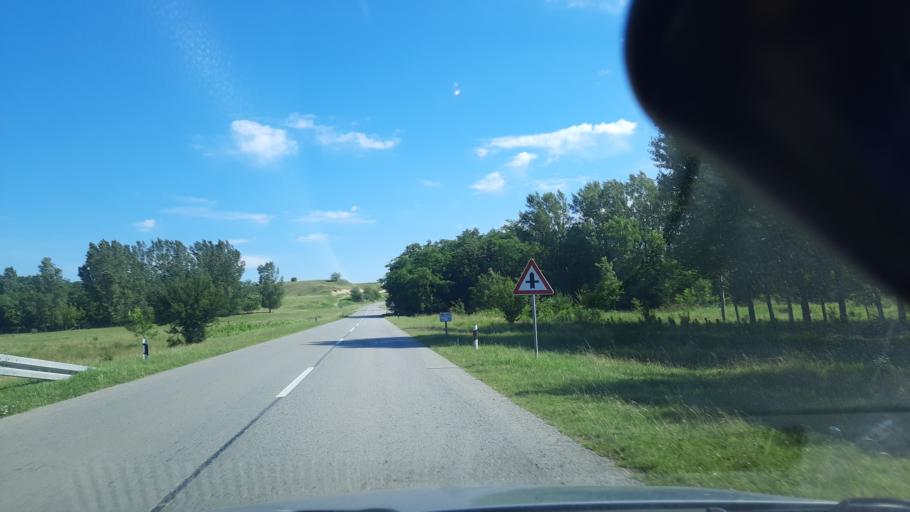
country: RO
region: Caras-Severin
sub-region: Comuna Socol
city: Socol
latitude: 44.8605
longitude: 21.3070
